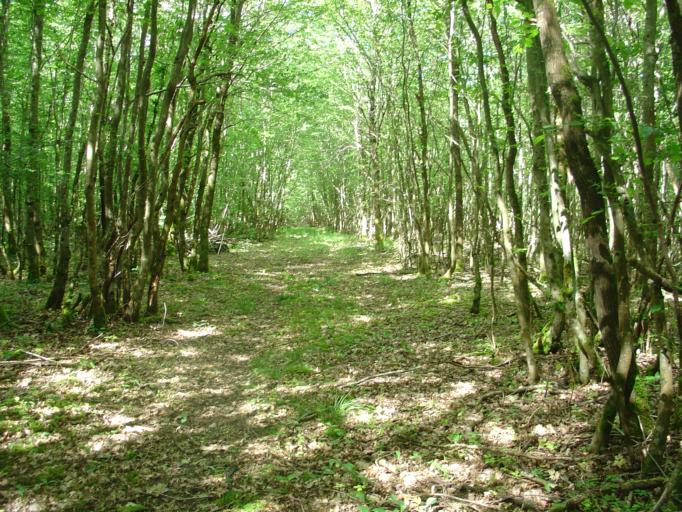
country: FR
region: Lorraine
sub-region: Departement de Meurthe-et-Moselle
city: Toul
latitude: 48.7906
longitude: 5.8828
